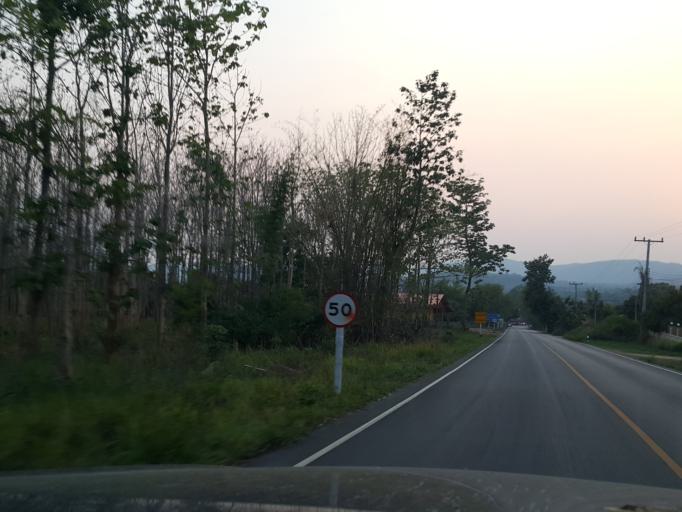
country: TH
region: Lamphun
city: Thung Hua Chang
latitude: 17.8770
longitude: 99.0670
